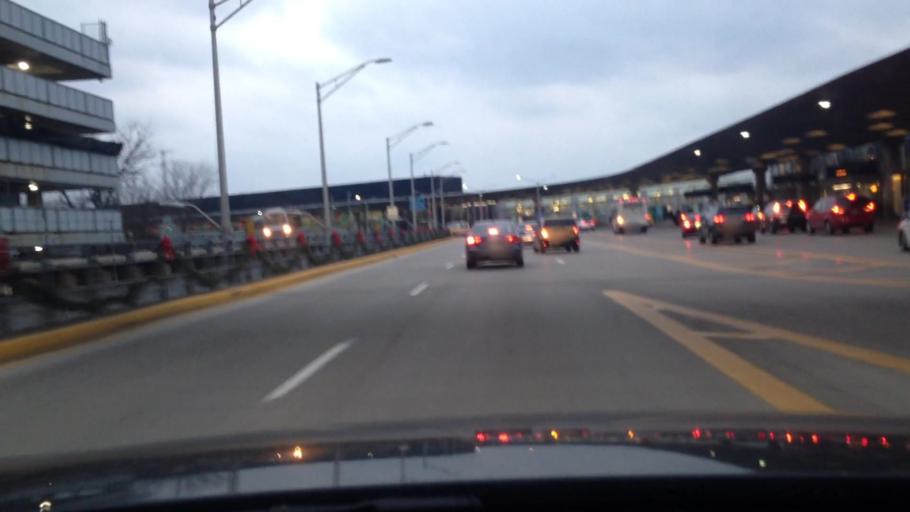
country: US
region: Illinois
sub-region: Cook County
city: Rosemont
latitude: 41.9790
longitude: -87.9058
